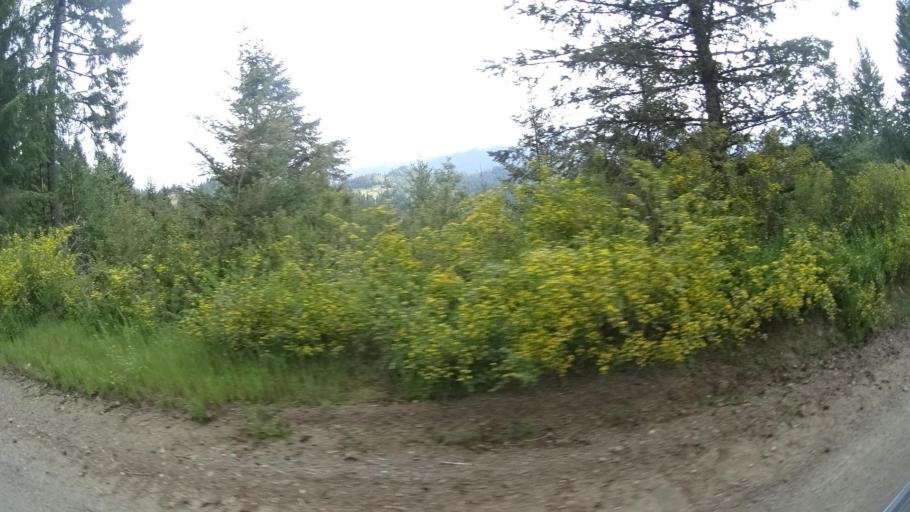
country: US
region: California
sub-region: Humboldt County
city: Redway
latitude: 40.2418
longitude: -123.7642
